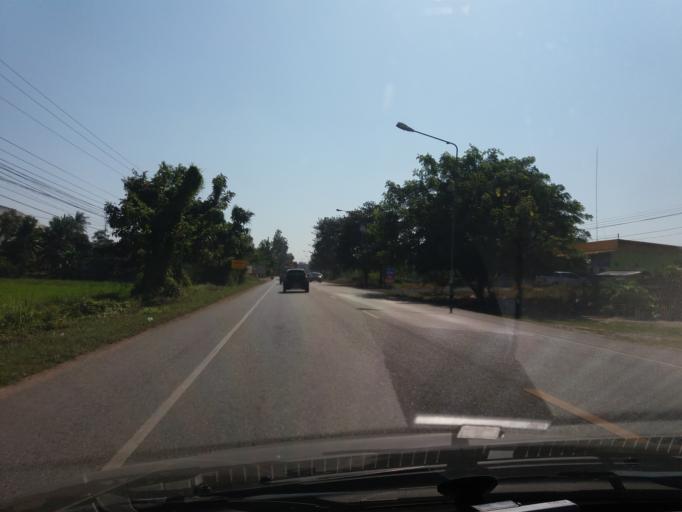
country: TH
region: Kamphaeng Phet
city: Khlong Khlung
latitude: 16.1763
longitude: 99.7911
